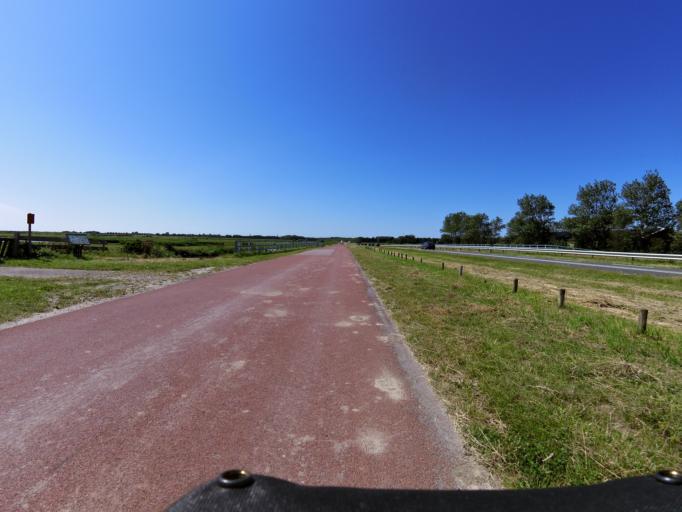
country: NL
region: South Holland
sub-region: Gemeente Goeree-Overflakkee
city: Goedereede
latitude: 51.8142
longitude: 3.9654
